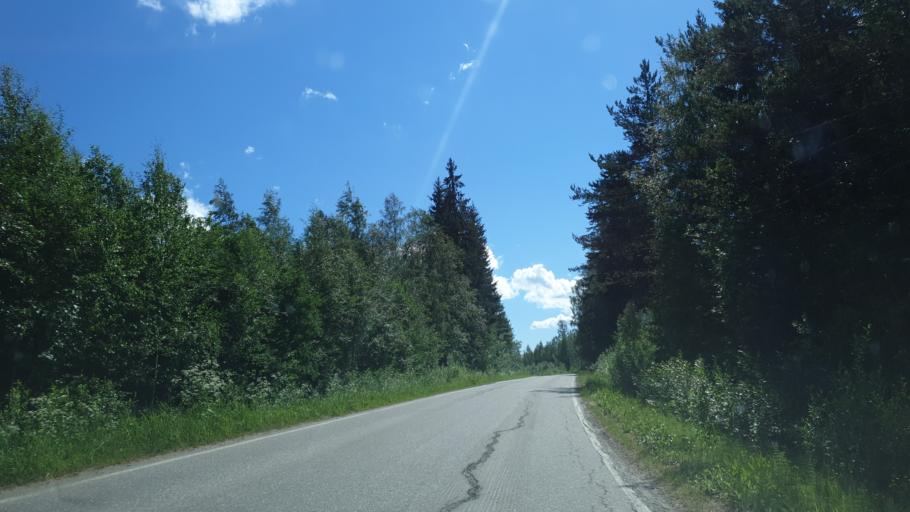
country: FI
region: Northern Savo
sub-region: Koillis-Savo
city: Kaavi
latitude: 62.9942
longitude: 28.5046
